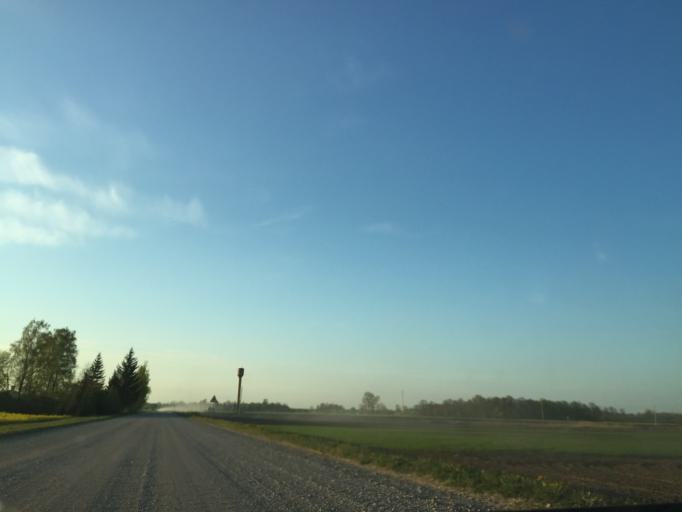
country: LV
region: Bauskas Rajons
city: Bauska
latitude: 56.3285
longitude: 24.1959
